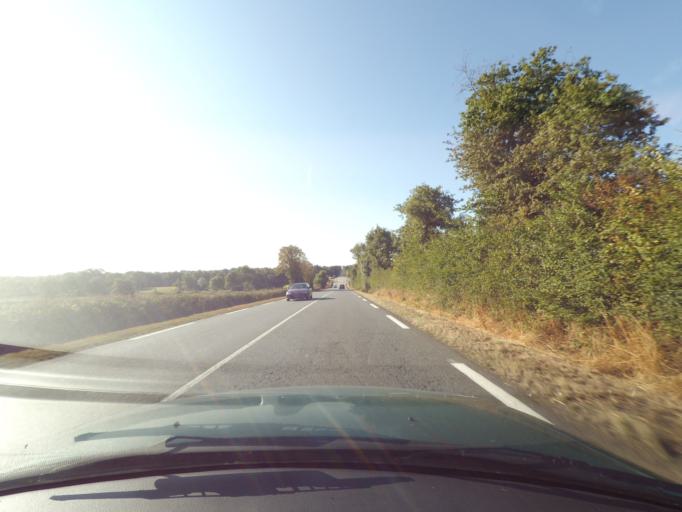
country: FR
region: Poitou-Charentes
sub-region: Departement des Deux-Sevres
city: Viennay
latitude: 46.7112
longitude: -0.2892
